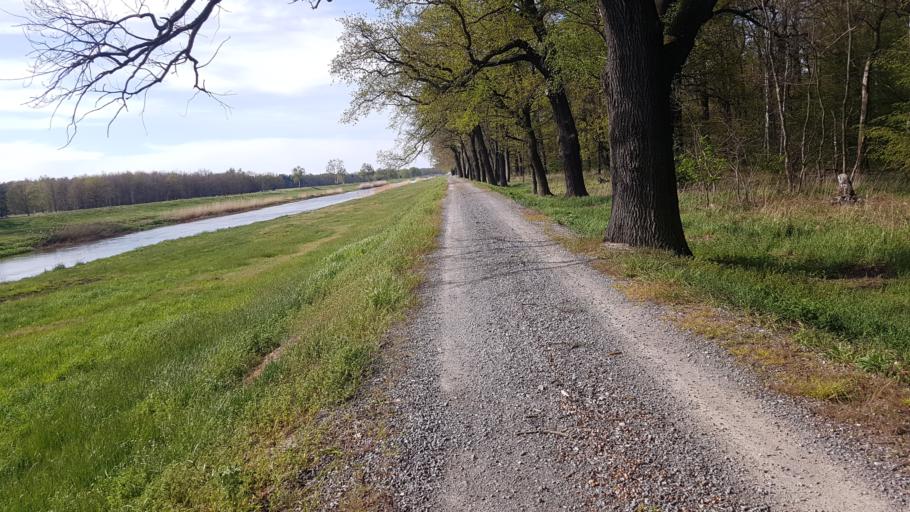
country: DE
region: Brandenburg
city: Falkenberg
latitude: 51.6240
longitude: 13.2866
